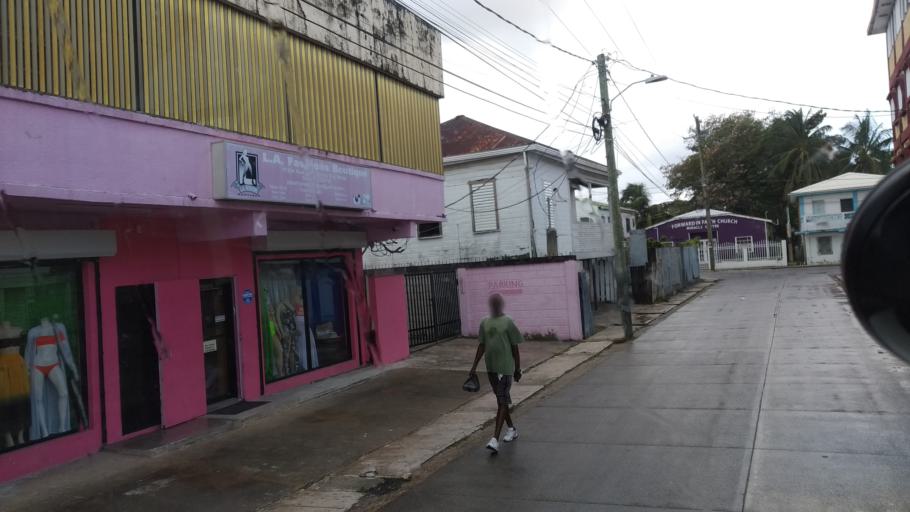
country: BZ
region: Belize
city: Belize City
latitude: 17.5008
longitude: -88.1902
